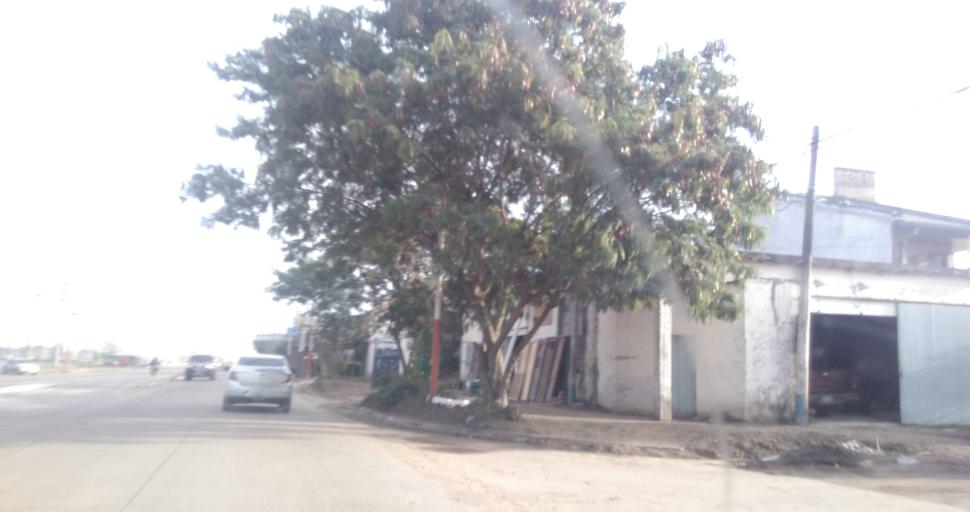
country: AR
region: Chaco
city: Resistencia
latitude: -27.4759
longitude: -59.0017
